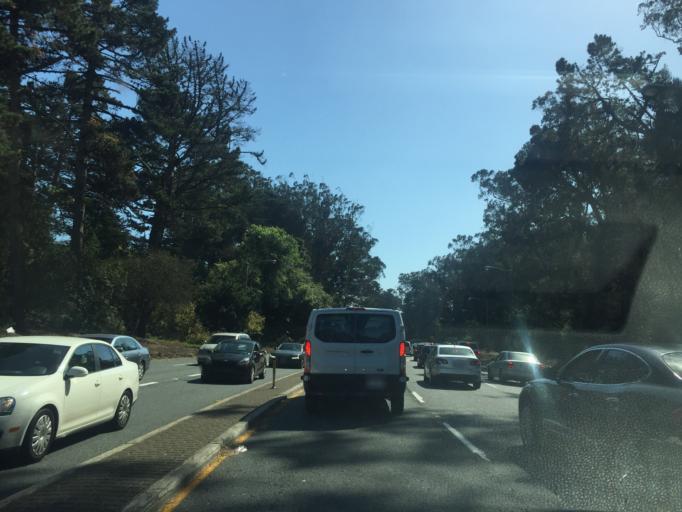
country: US
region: California
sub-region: San Francisco County
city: San Francisco
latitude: 37.7693
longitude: -122.4786
